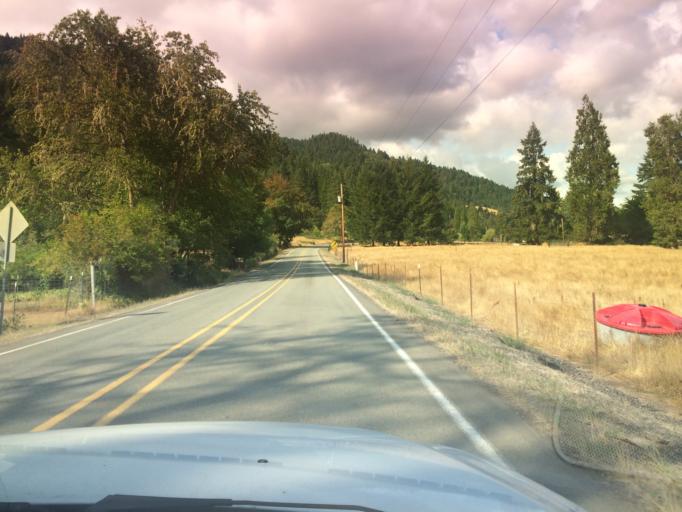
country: US
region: Oregon
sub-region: Douglas County
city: Sutherlin
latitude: 43.3642
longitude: -123.5773
